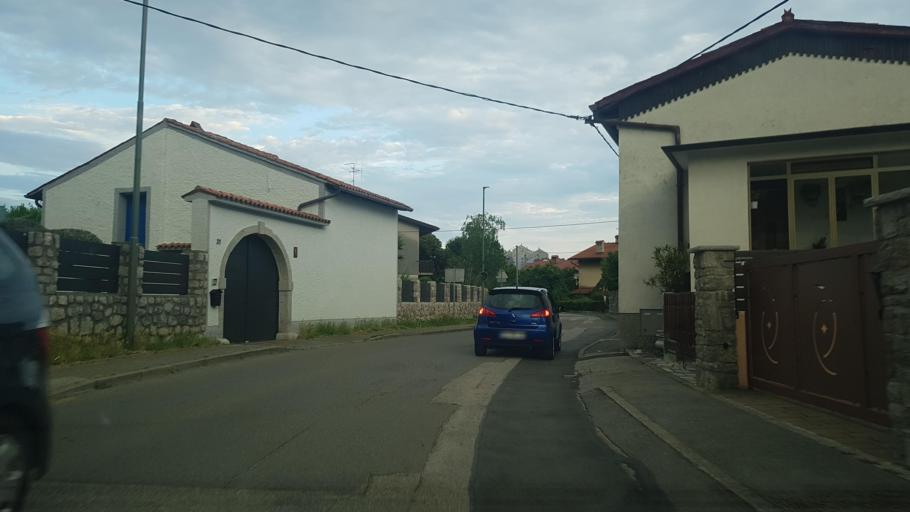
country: SI
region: Nova Gorica
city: Solkan
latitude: 45.9683
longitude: 13.6494
